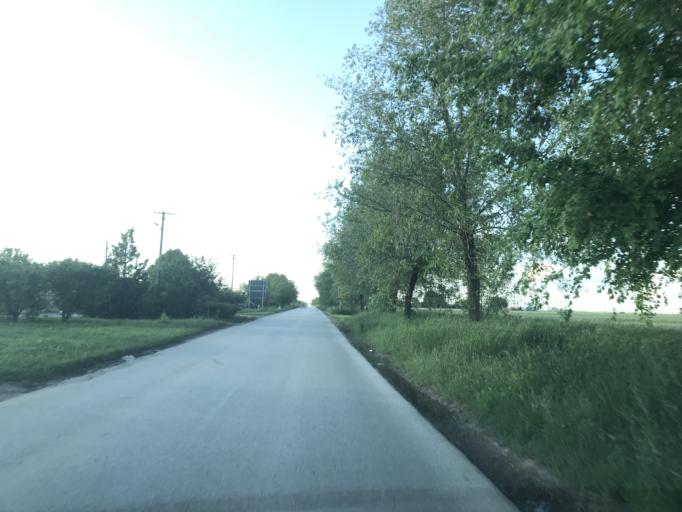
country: RS
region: Autonomna Pokrajina Vojvodina
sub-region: Srednjebanatski Okrug
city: Zrenjanin
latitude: 45.4082
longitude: 20.3928
